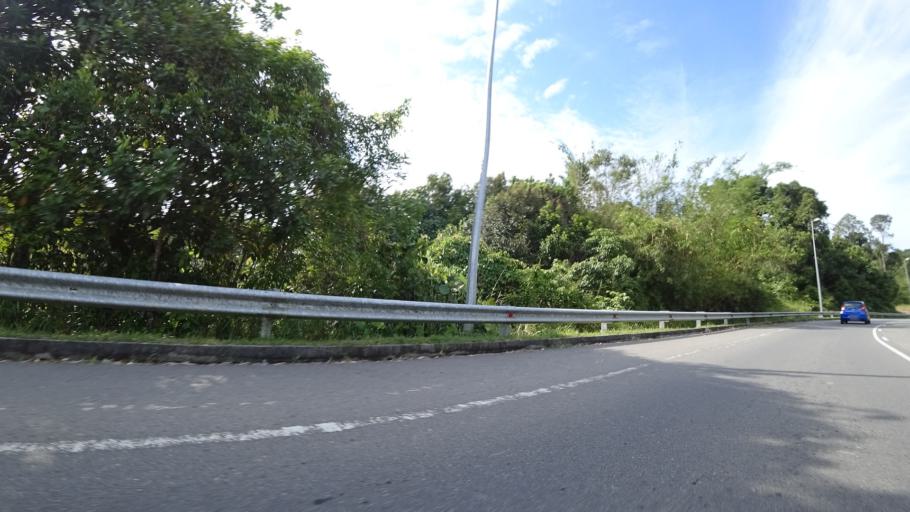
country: BN
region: Brunei and Muara
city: Bandar Seri Begawan
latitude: 4.8823
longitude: 114.8018
